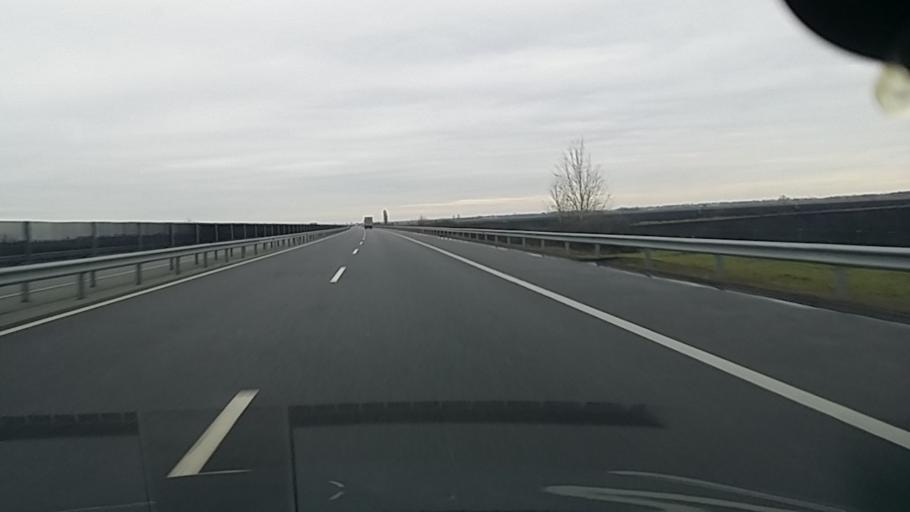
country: HU
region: Hajdu-Bihar
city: Gorbehaza
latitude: 47.8302
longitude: 21.3302
